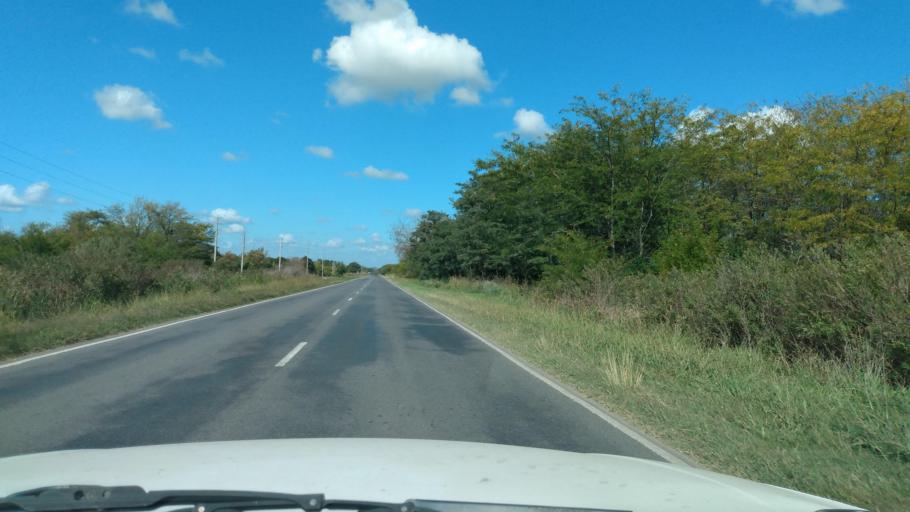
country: AR
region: Buenos Aires
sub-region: Partido de Mercedes
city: Mercedes
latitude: -34.6916
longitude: -59.4044
